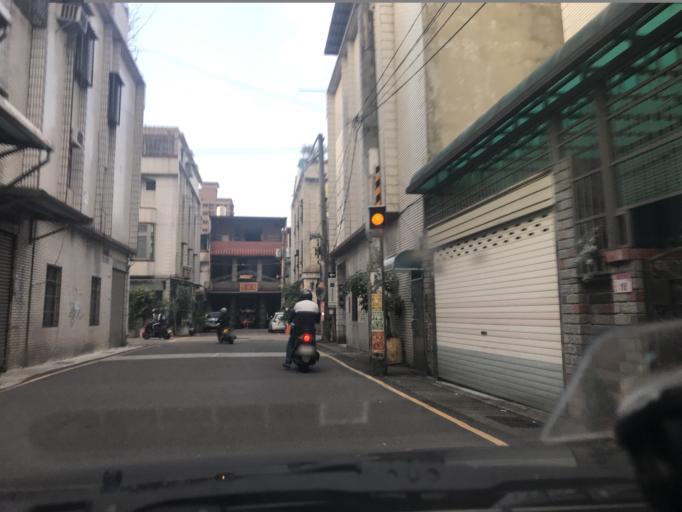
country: TW
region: Taiwan
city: Taoyuan City
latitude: 24.9545
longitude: 121.2309
